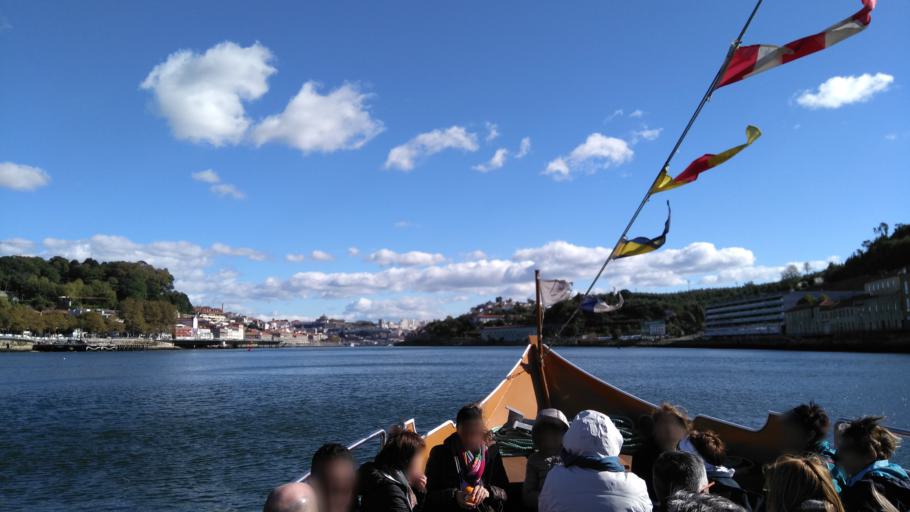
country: PT
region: Porto
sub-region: Vila Nova de Gaia
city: Vila Nova de Gaia
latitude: 41.1468
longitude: -8.6374
